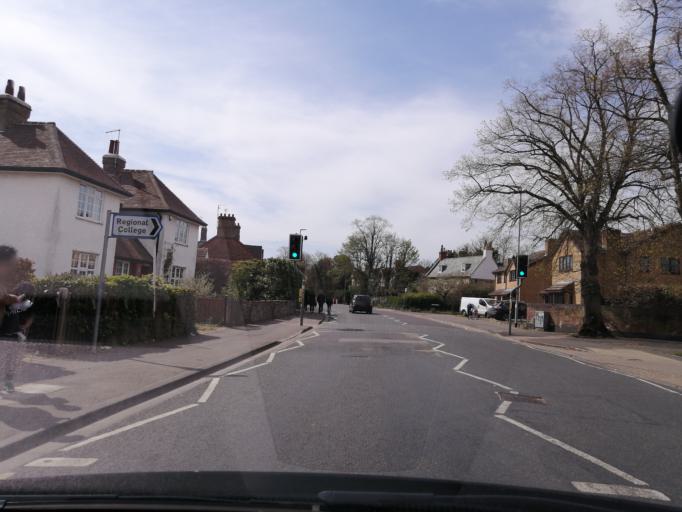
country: GB
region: England
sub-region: Peterborough
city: Peterborough
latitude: 52.5857
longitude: -0.2264
